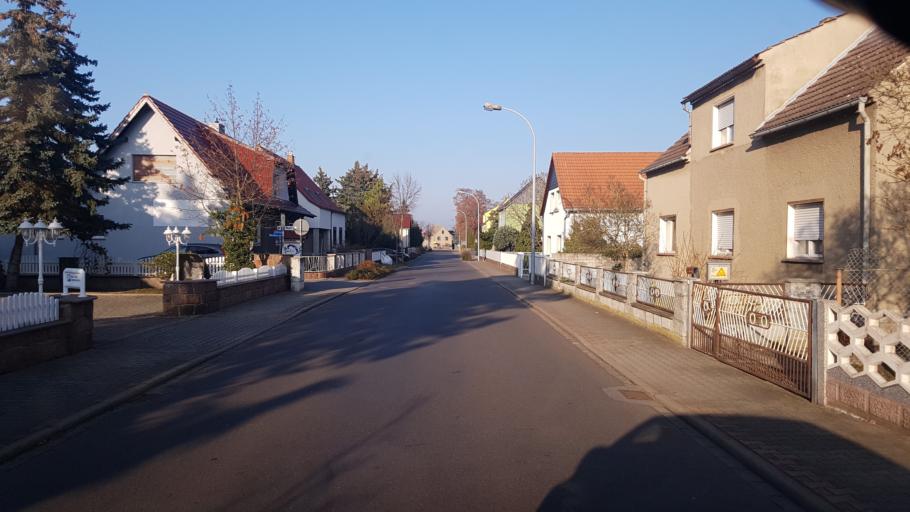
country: DE
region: Brandenburg
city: Tettau
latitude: 51.4287
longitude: 13.7284
